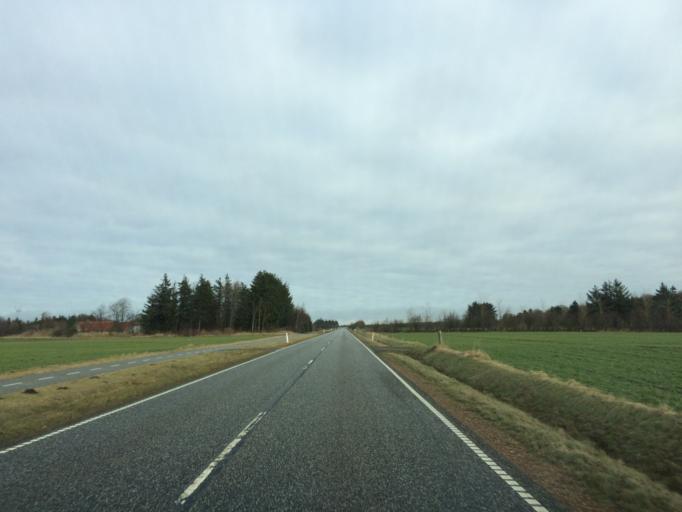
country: DK
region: Central Jutland
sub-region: Holstebro Kommune
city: Ulfborg
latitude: 56.3505
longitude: 8.3685
